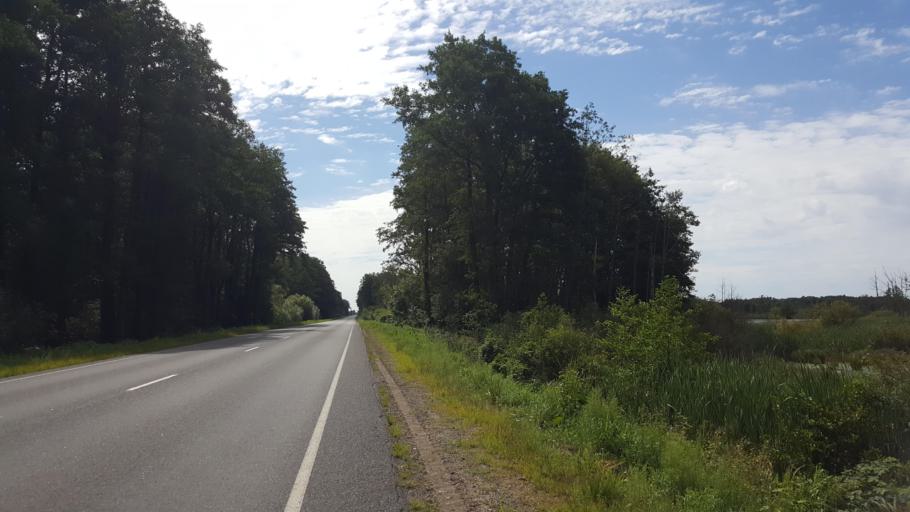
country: BY
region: Brest
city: Zhabinka
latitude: 52.2719
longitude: 23.9546
